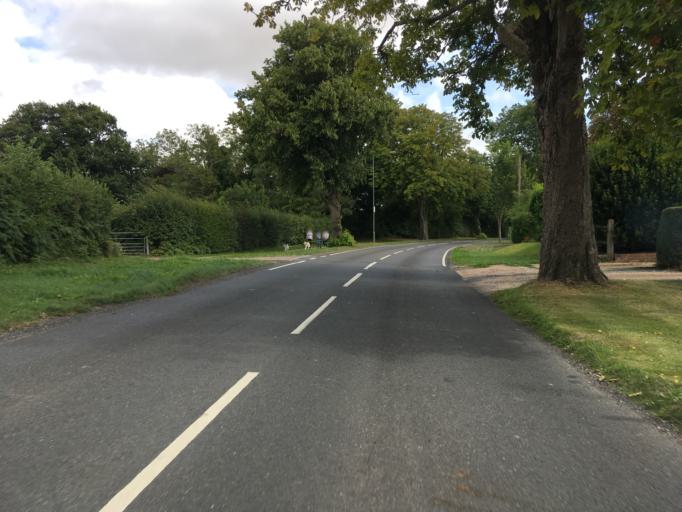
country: GB
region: England
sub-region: Kent
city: Tenterden
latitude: 51.0683
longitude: 0.7058
